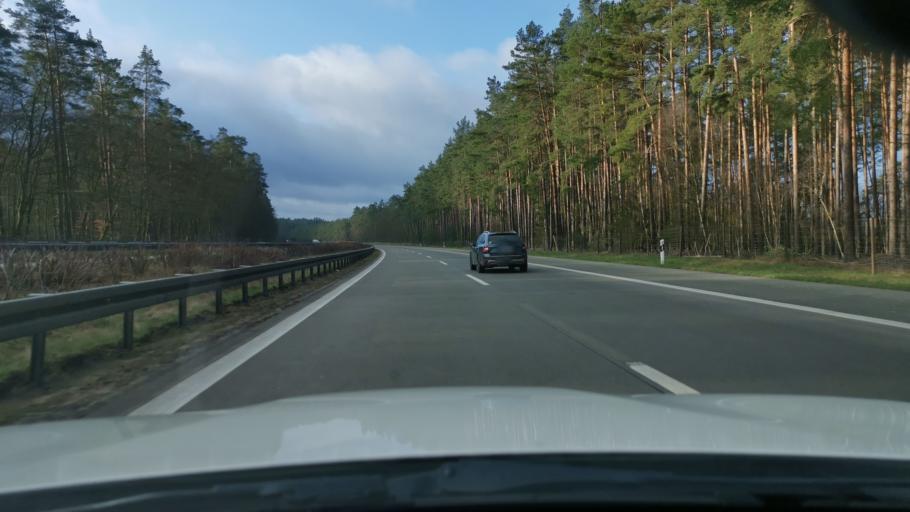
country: DE
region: Mecklenburg-Vorpommern
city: Krakow am See
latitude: 53.5725
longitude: 12.3202
